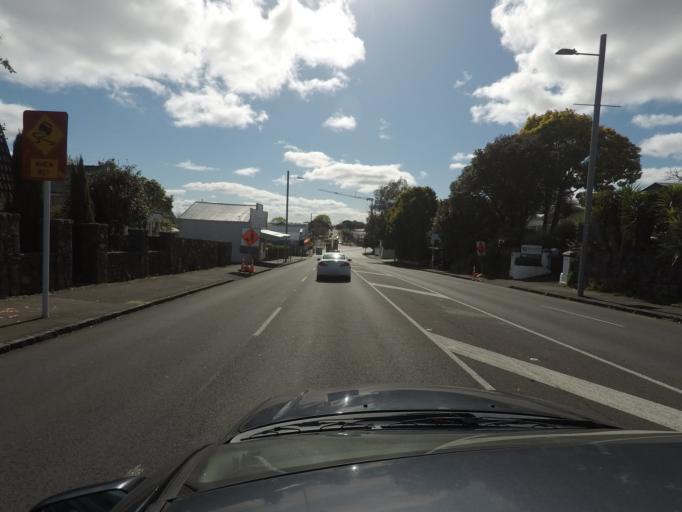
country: NZ
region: Auckland
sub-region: Auckland
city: Rosebank
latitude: -36.8832
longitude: 174.7167
